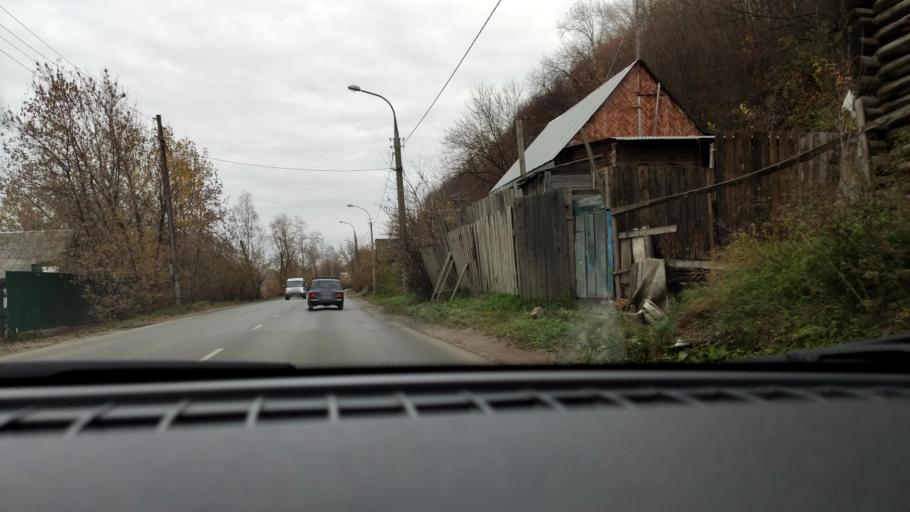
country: RU
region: Perm
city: Perm
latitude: 58.0516
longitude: 56.3280
